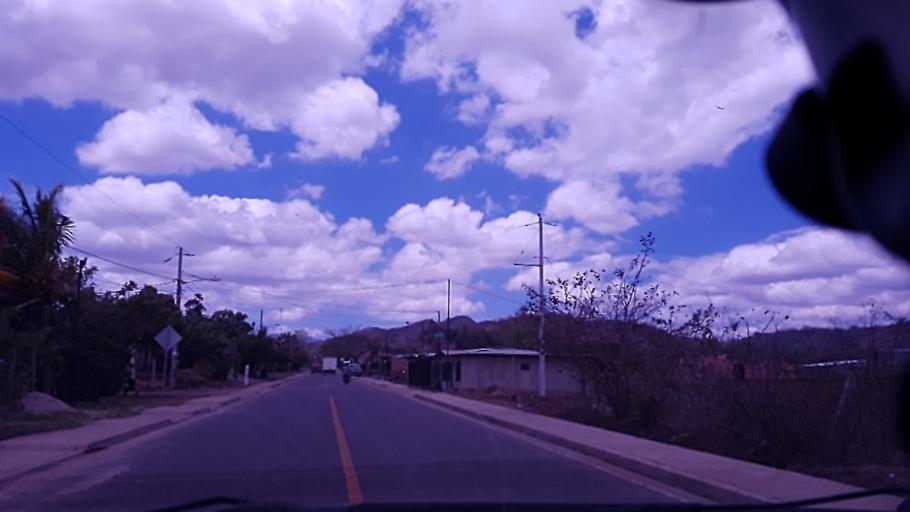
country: NI
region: Esteli
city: Condega
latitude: 13.3764
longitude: -86.3910
